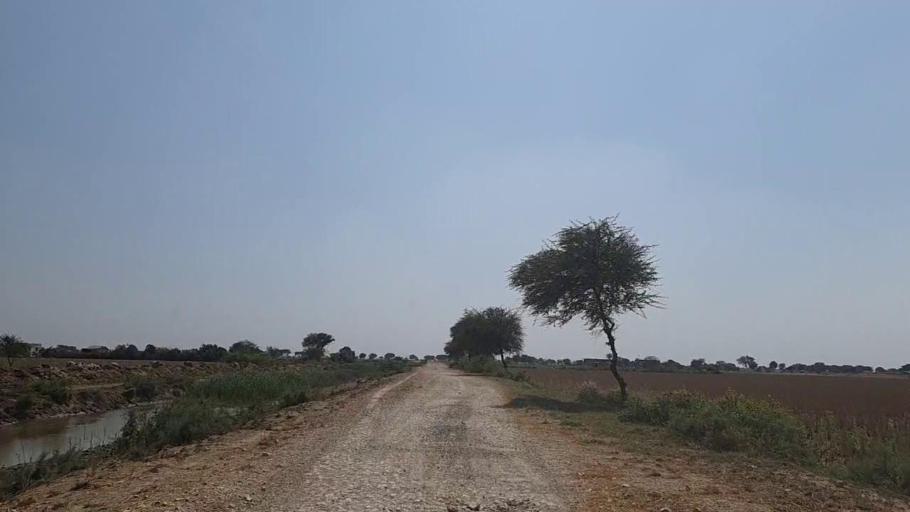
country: PK
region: Sindh
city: Jati
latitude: 24.5394
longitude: 68.3153
